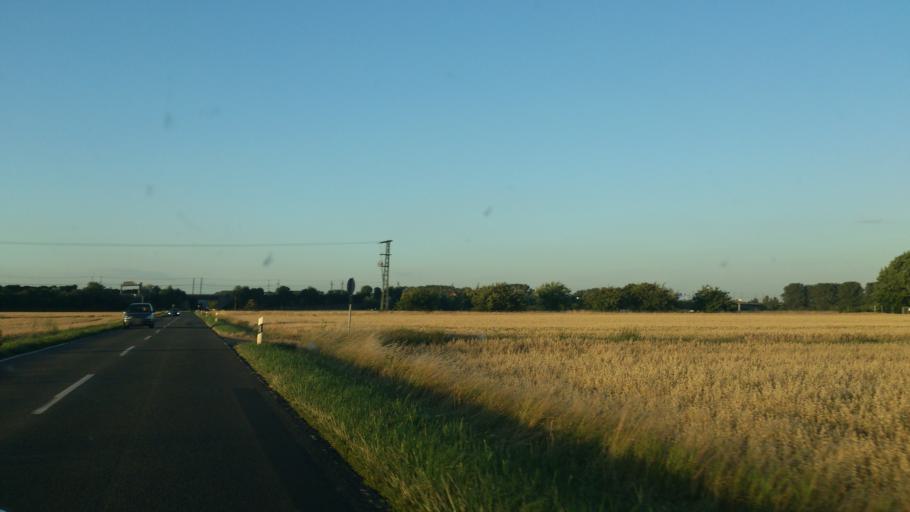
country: DE
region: Hesse
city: Raunheim
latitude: 50.0268
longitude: 8.4526
